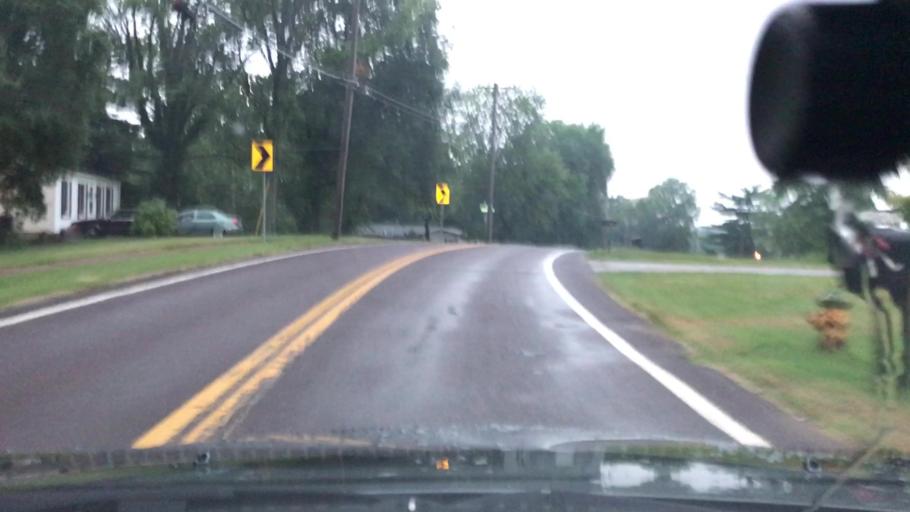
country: US
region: Missouri
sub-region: Saint Louis County
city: Maryland Heights
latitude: 38.6935
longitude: -90.4600
